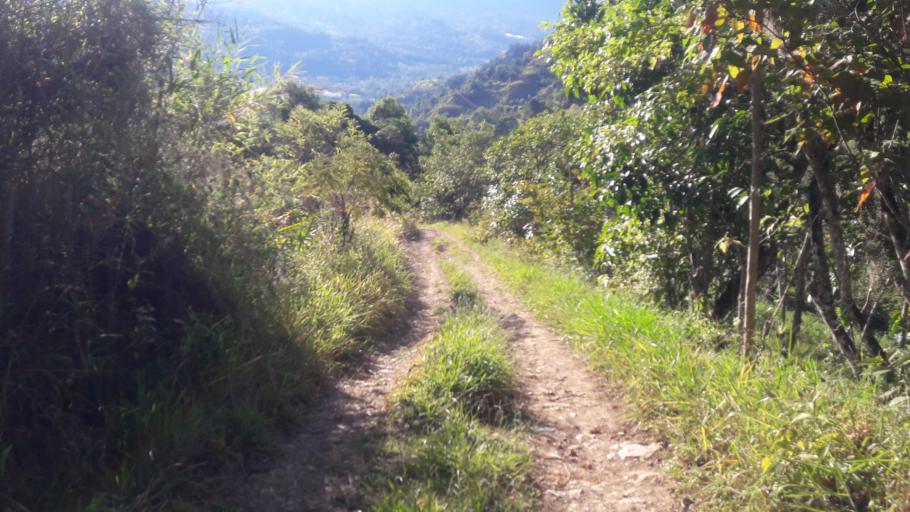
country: CO
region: Cundinamarca
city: Tenza
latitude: 5.0884
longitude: -73.4182
